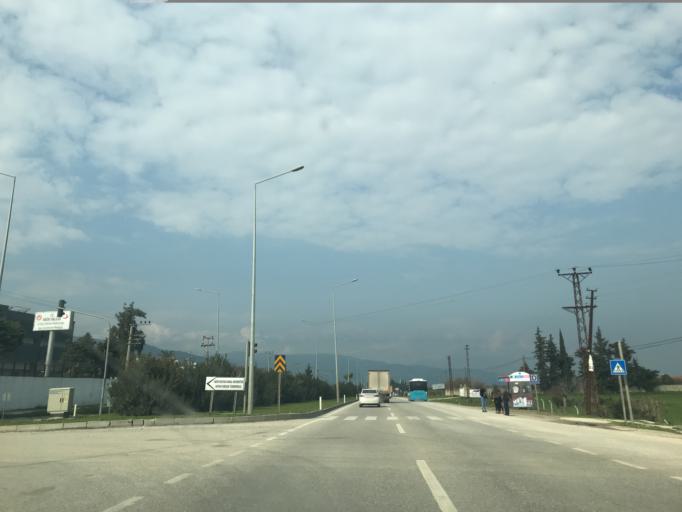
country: TR
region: Hatay
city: Anayazi
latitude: 36.3067
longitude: 36.2003
